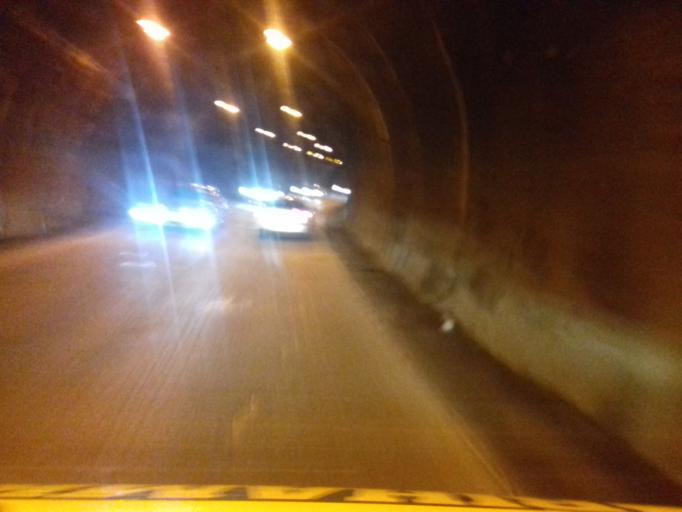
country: BA
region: Federation of Bosnia and Herzegovina
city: Jablanica
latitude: 43.6830
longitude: 17.8092
